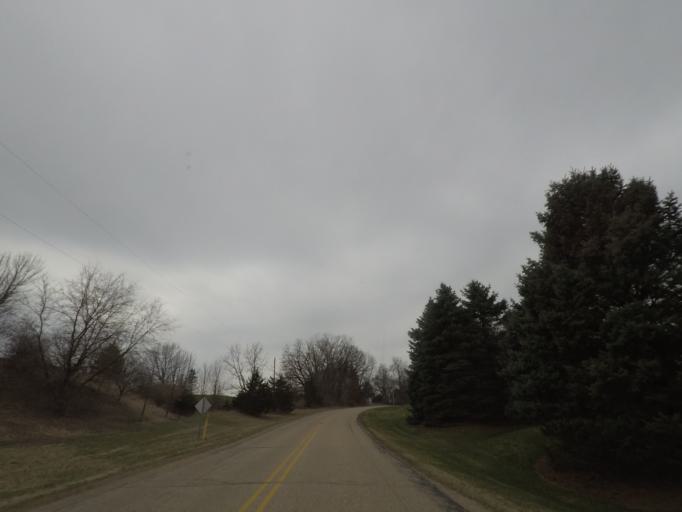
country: US
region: Wisconsin
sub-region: Dane County
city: Middleton
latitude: 43.1086
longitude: -89.5413
